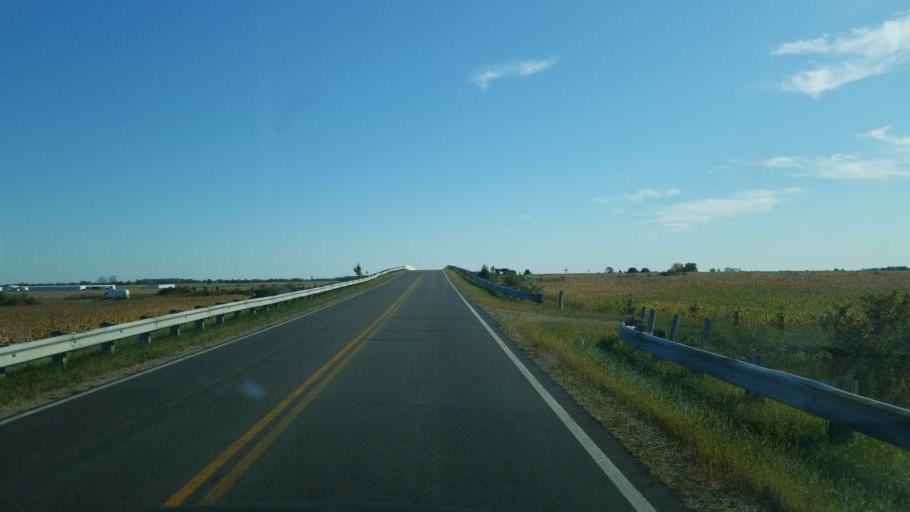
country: US
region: Ohio
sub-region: Madison County
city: Choctaw Lake
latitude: 39.9435
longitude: -83.4729
